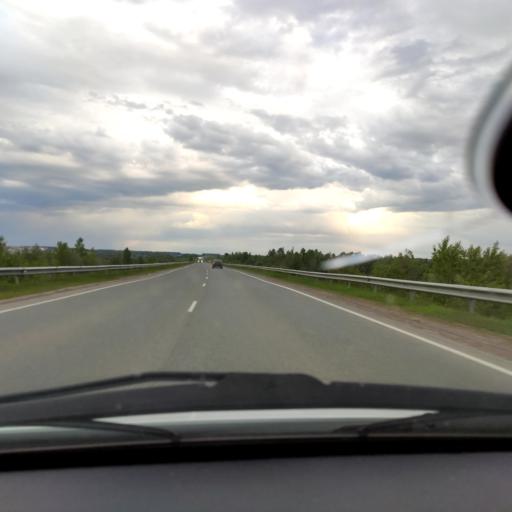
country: RU
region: Bashkortostan
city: Dyurtyuli
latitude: 55.5215
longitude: 54.8395
